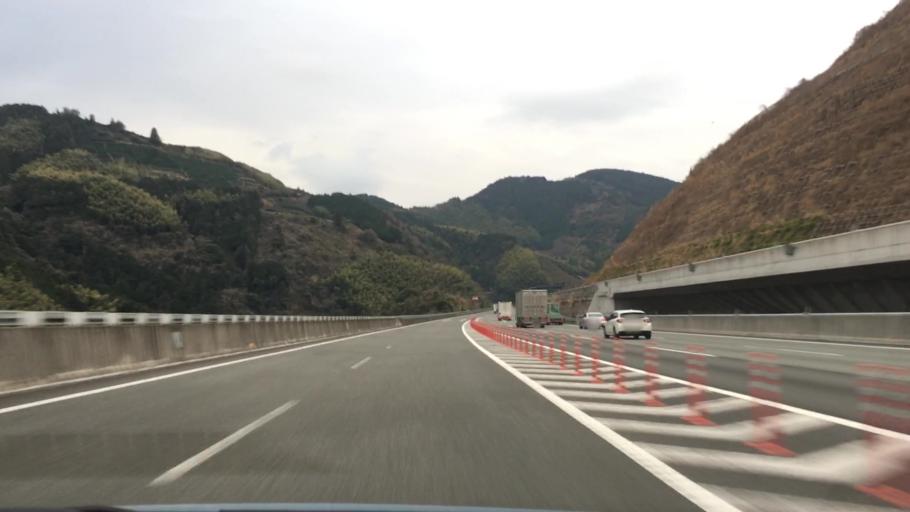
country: JP
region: Shizuoka
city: Shizuoka-shi
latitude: 35.0721
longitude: 138.4587
